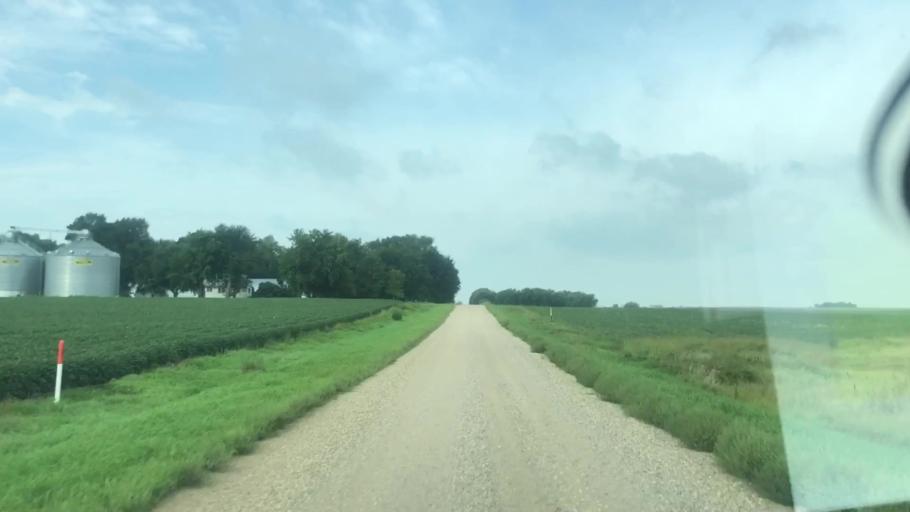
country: US
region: Iowa
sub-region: Lyon County
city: George
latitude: 43.2723
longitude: -95.9702
